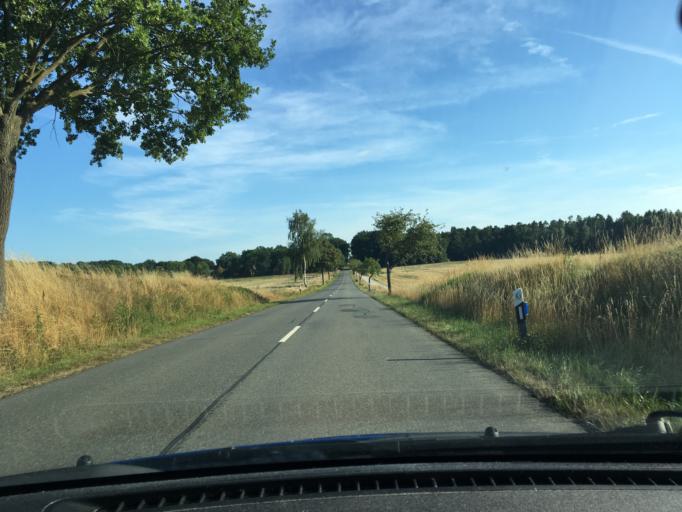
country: DE
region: Lower Saxony
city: Altenmedingen
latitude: 53.1841
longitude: 10.6298
